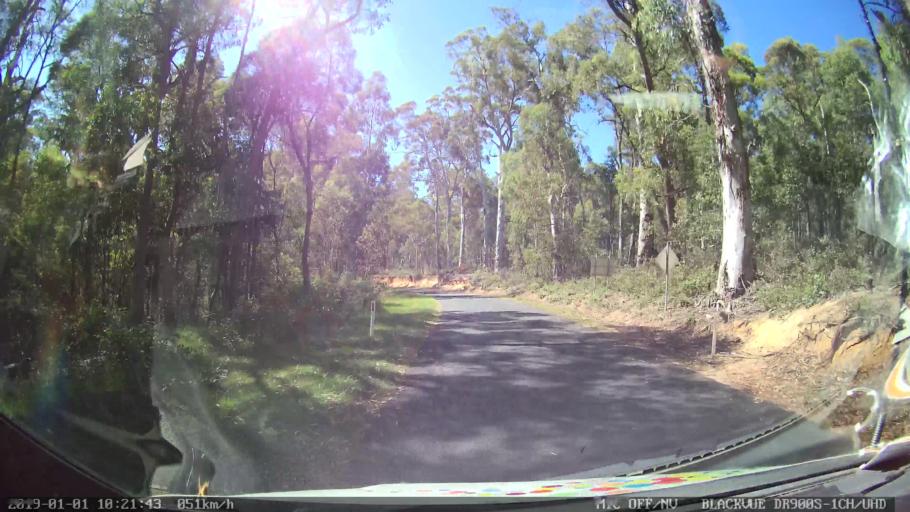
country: AU
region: New South Wales
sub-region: Snowy River
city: Jindabyne
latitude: -36.0774
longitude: 148.1972
